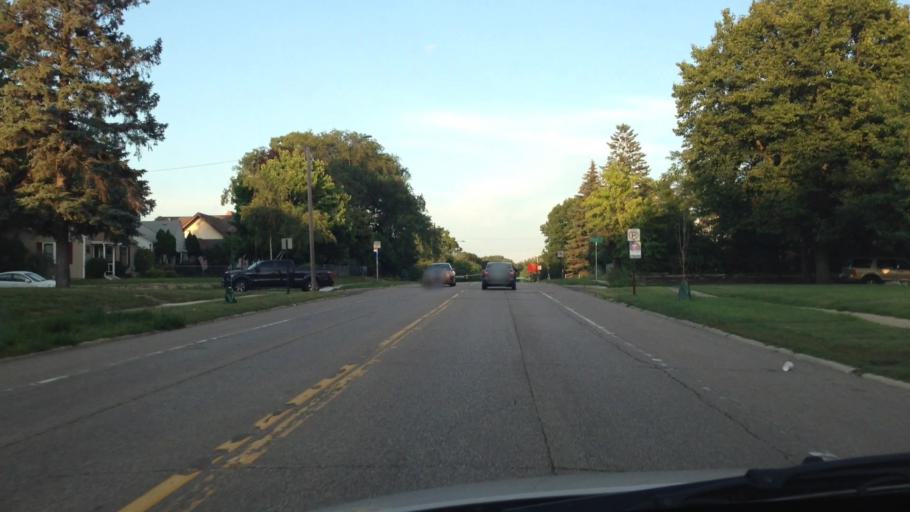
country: US
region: Minnesota
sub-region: Hennepin County
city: Saint Louis Park
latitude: 44.9496
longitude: -93.3639
